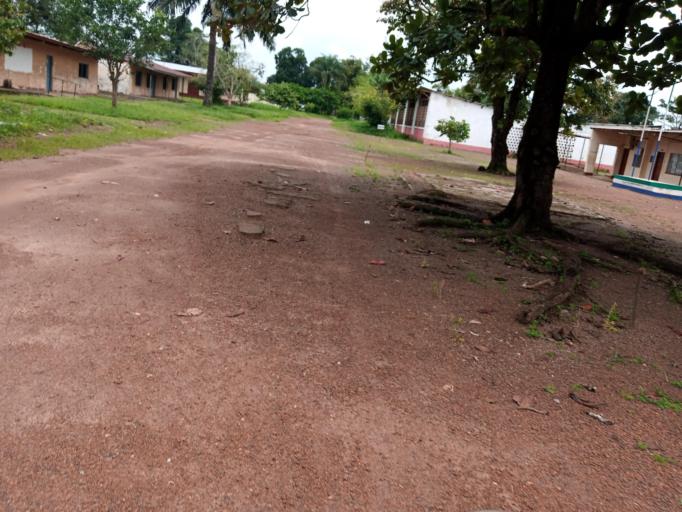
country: SL
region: Southern Province
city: Largo
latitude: 8.1979
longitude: -12.0630
